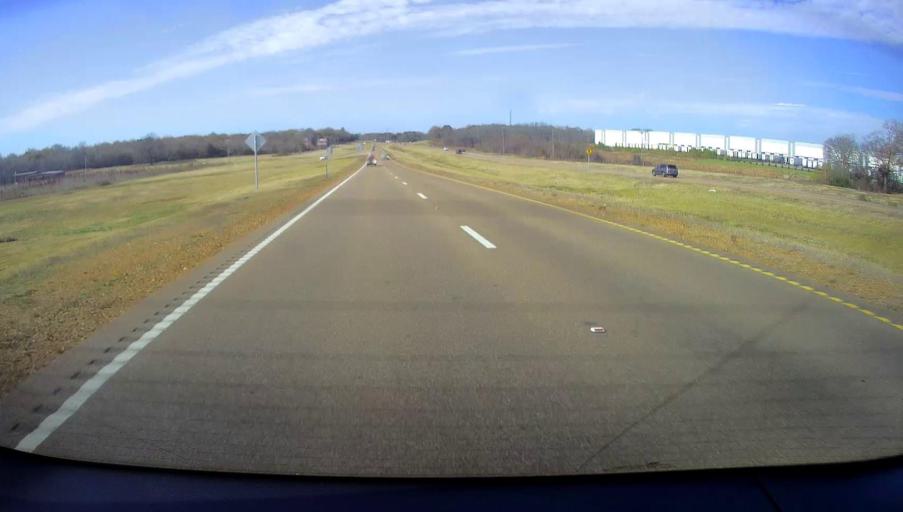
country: US
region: Tennessee
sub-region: Fayette County
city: Piperton
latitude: 34.9864
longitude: -89.5993
